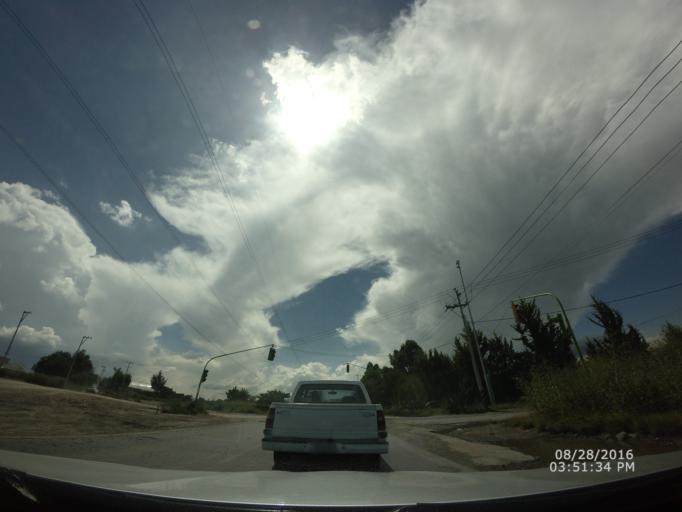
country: MX
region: Hidalgo
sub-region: Mineral de la Reforma
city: Los Tuzos
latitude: 20.0368
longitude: -98.7419
